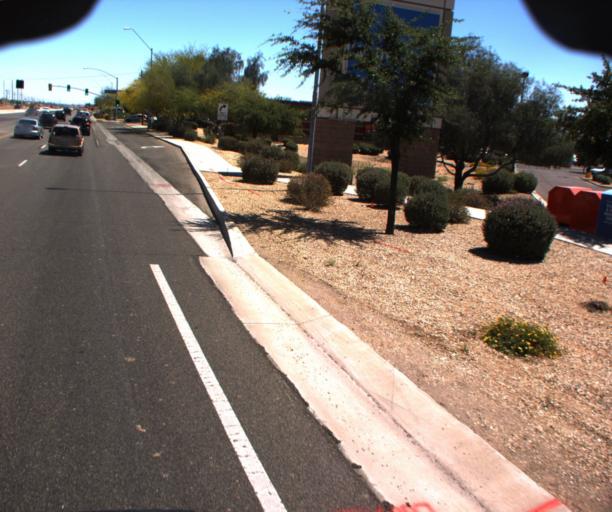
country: US
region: Arizona
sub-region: Maricopa County
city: Sun City West
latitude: 33.6430
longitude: -112.3561
